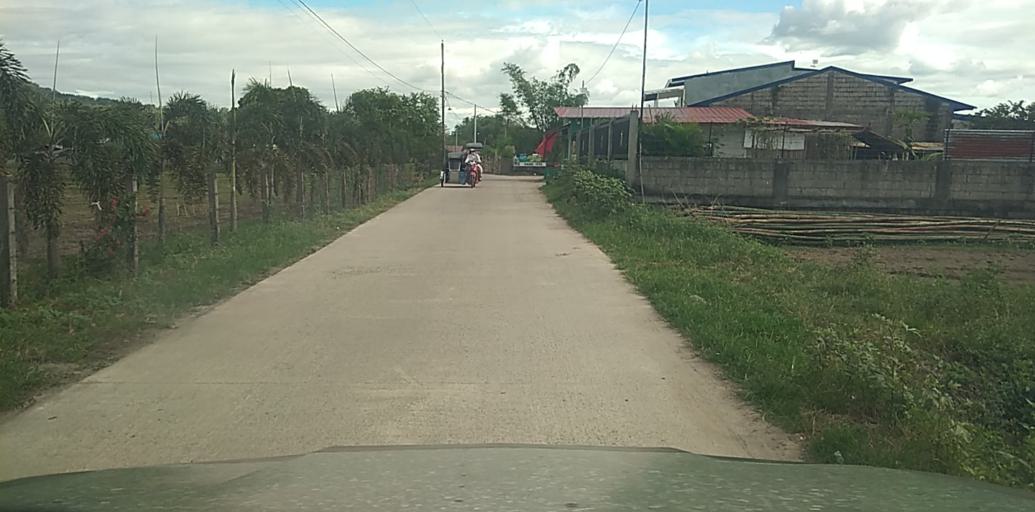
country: PH
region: Central Luzon
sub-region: Province of Pampanga
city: Panlinlang
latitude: 15.1859
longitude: 120.6942
